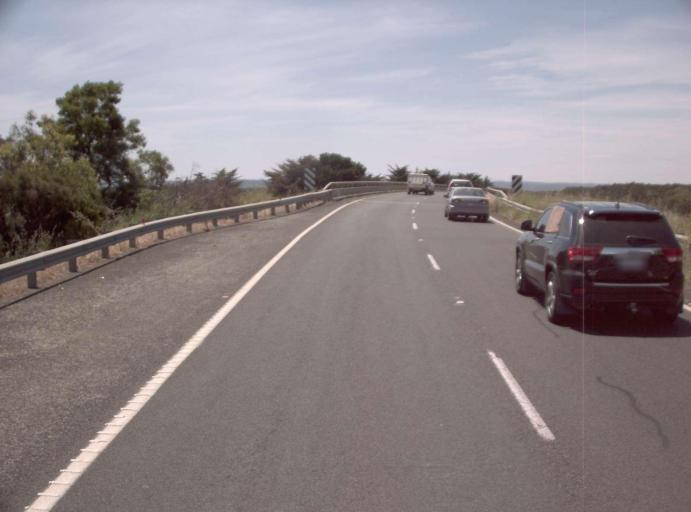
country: AU
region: Victoria
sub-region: Latrobe
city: Morwell
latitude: -38.2310
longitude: 146.4561
